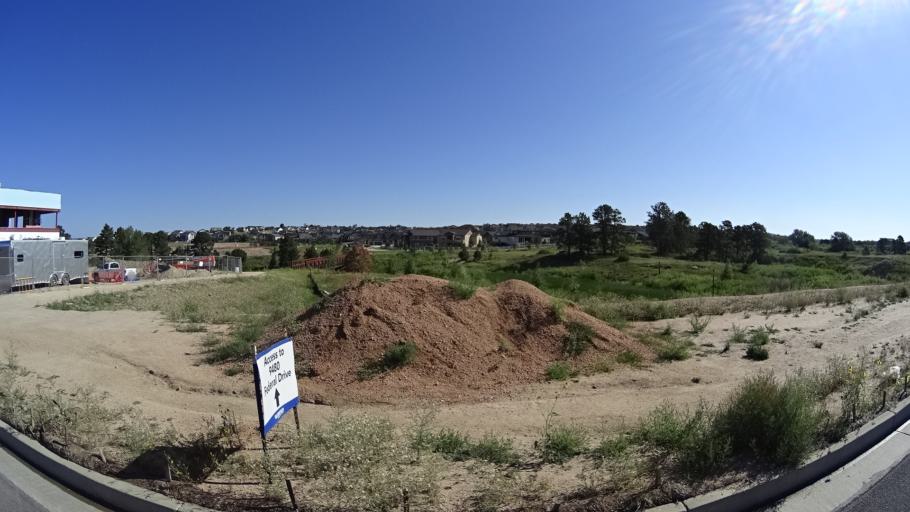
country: US
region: Colorado
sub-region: El Paso County
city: Gleneagle
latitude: 38.9973
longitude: -104.8053
